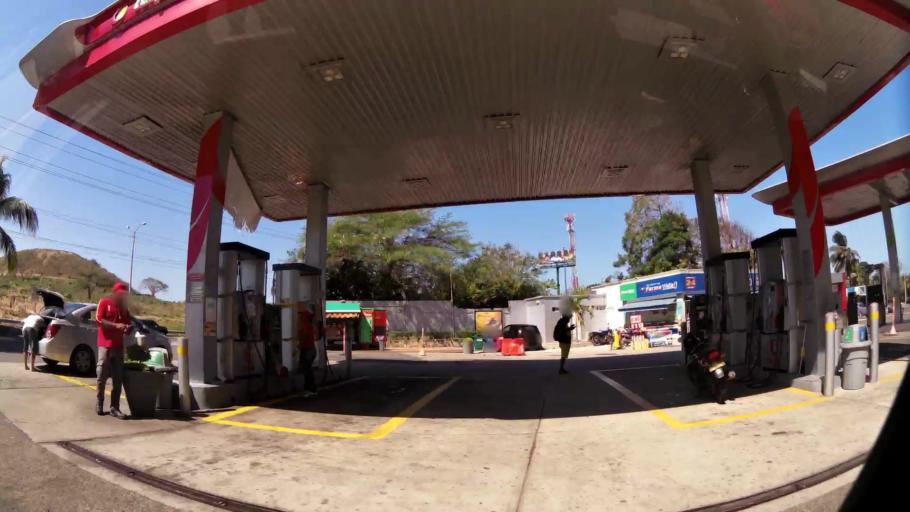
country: CO
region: Atlantico
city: Barranquilla
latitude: 11.0154
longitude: -74.8467
